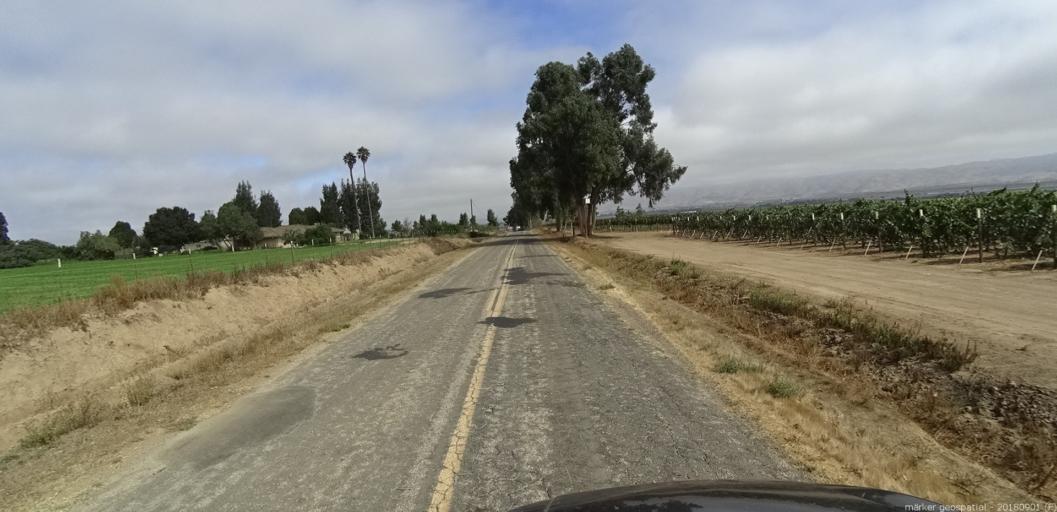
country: US
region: California
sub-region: Monterey County
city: Soledad
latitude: 36.3707
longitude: -121.3367
